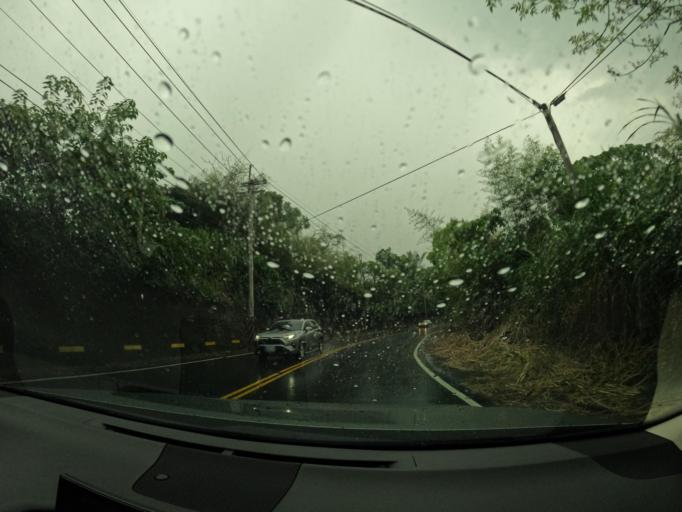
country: TW
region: Taiwan
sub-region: Nantou
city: Nantou
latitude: 23.8854
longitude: 120.7445
